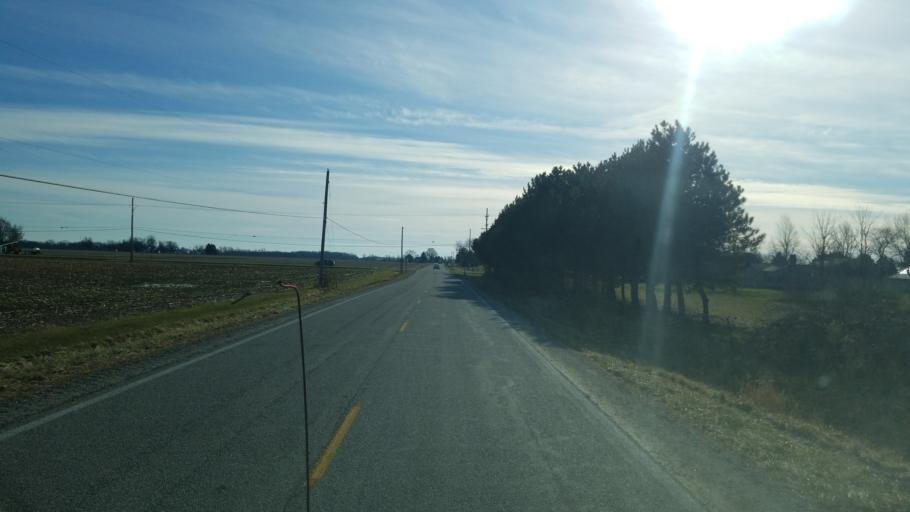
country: US
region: Ohio
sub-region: Sandusky County
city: Stony Prairie
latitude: 41.3502
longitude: -83.2235
